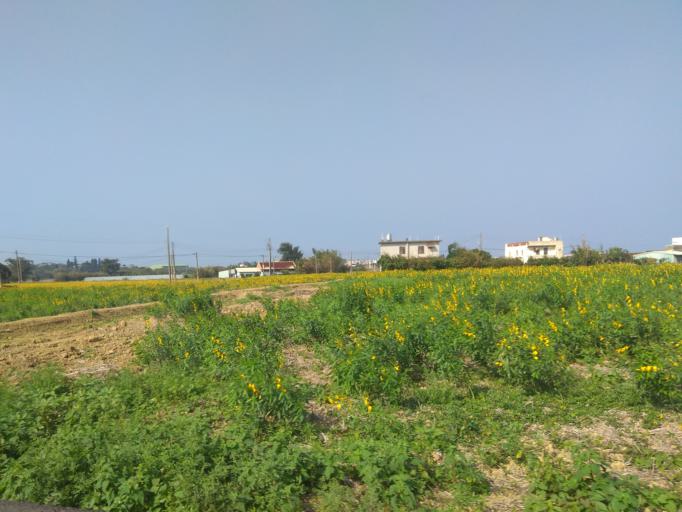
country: TW
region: Taiwan
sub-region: Hsinchu
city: Zhubei
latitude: 24.9978
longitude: 121.0429
